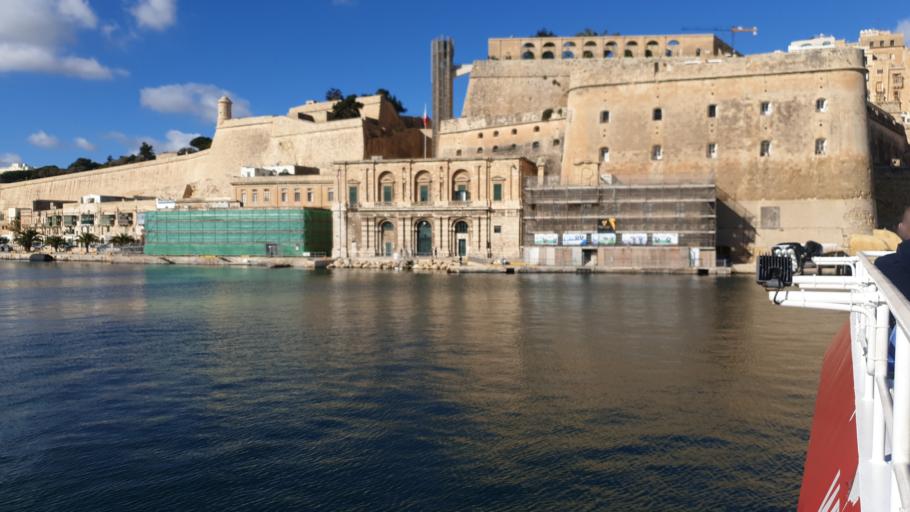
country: MT
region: Il-Birgu
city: Vittoriosa
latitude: 35.8936
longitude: 14.5141
